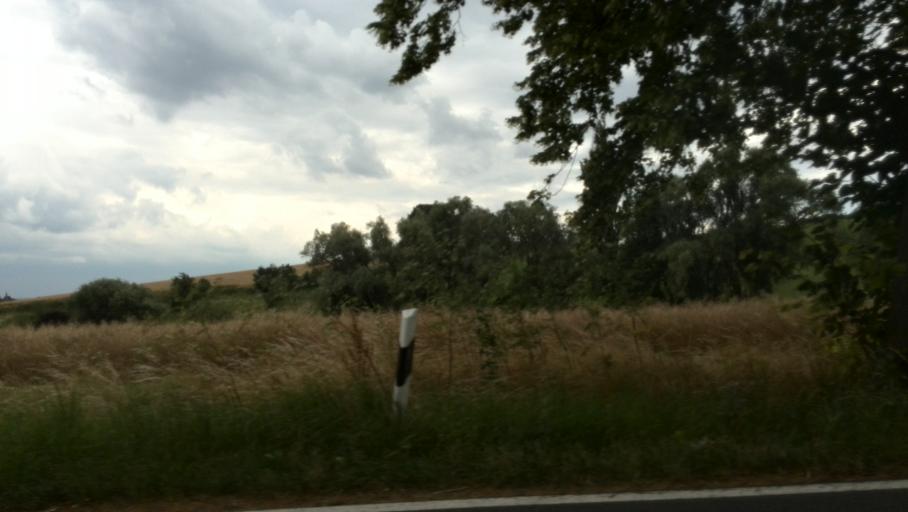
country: DE
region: Lower Saxony
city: Holle
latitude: 52.0805
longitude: 10.1694
